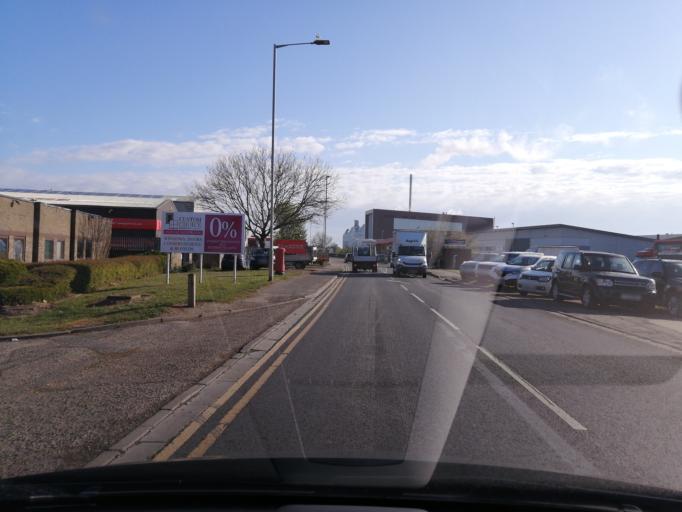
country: GB
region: England
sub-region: Peterborough
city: Peterborough
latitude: 52.5729
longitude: -0.2109
